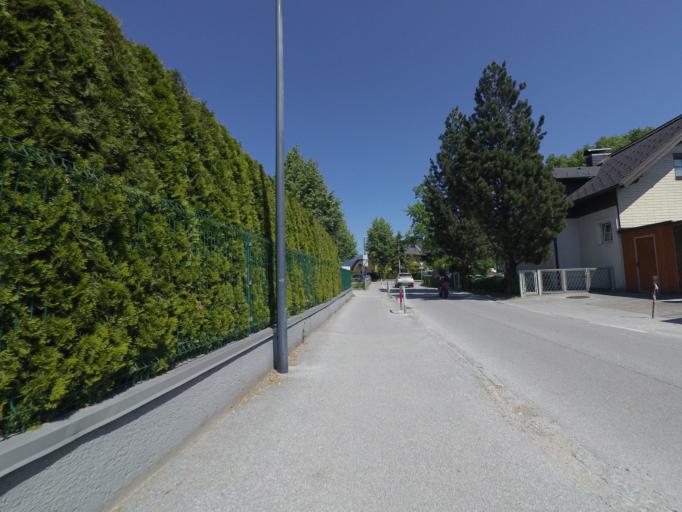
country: AT
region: Salzburg
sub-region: Politischer Bezirk Salzburg-Umgebung
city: Grodig
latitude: 47.7602
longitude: 13.0156
